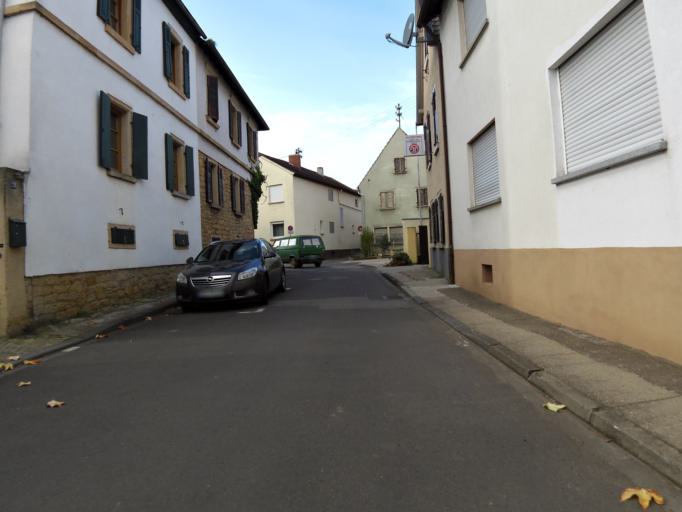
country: DE
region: Rheinland-Pfalz
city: Niederkirchen bei Deidesheim
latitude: 49.4146
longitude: 8.2130
